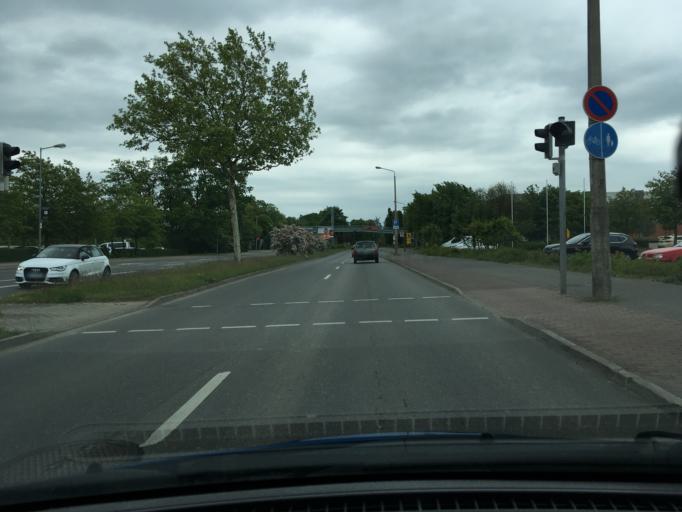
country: DE
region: Mecklenburg-Vorpommern
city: Wismar
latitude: 53.8868
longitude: 11.4472
